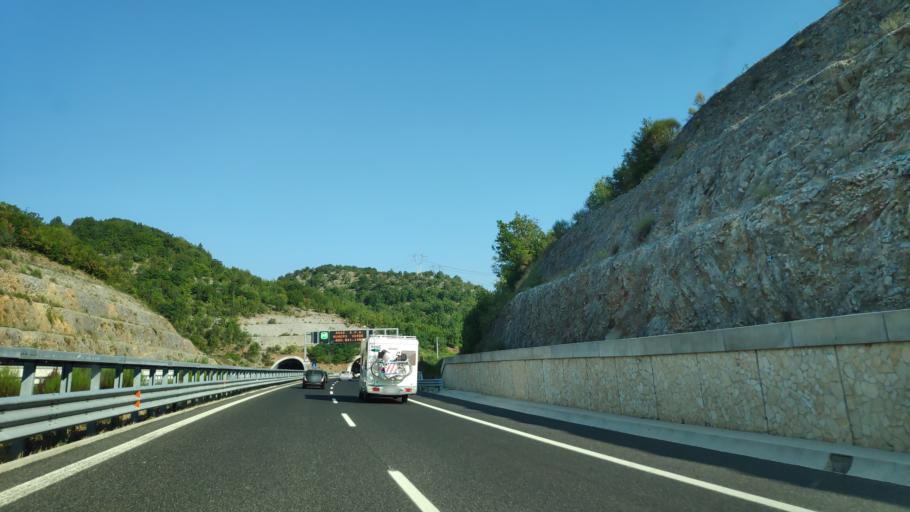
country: IT
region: Campania
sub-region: Provincia di Salerno
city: Casalbuono
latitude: 40.1994
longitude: 15.6885
